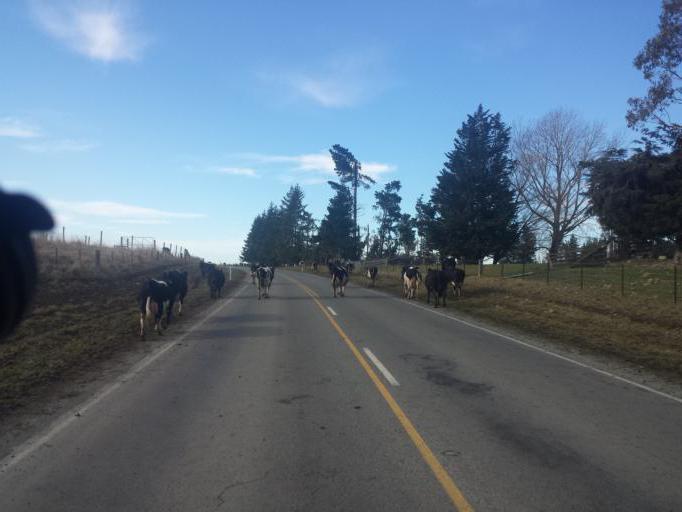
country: NZ
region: Canterbury
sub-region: Timaru District
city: Pleasant Point
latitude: -43.9716
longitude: 171.3091
